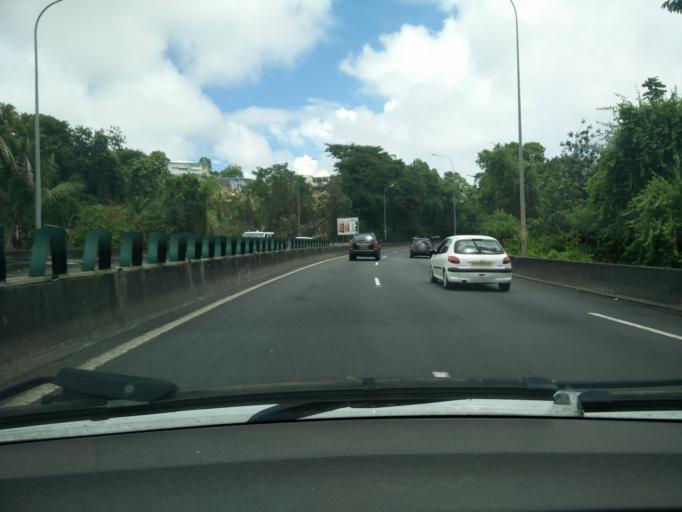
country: GP
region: Guadeloupe
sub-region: Guadeloupe
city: Pointe-a-Pitre
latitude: 16.2435
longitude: -61.5231
